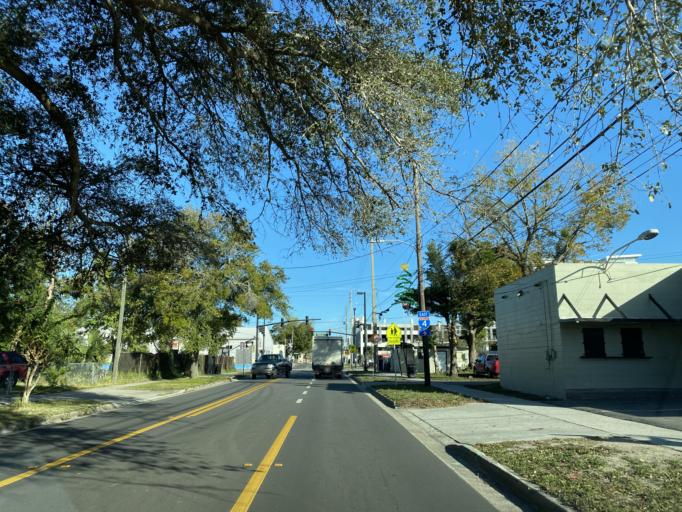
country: US
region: Florida
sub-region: Orange County
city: Orlando
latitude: 28.5450
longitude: -81.3891
